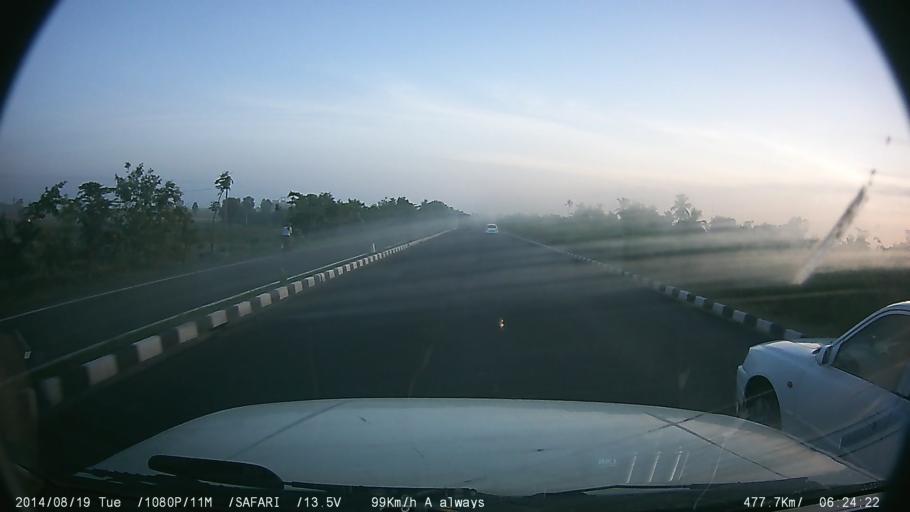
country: IN
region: Tamil Nadu
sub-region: Dharmapuri
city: Dharmapuri
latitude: 12.0512
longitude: 78.1069
